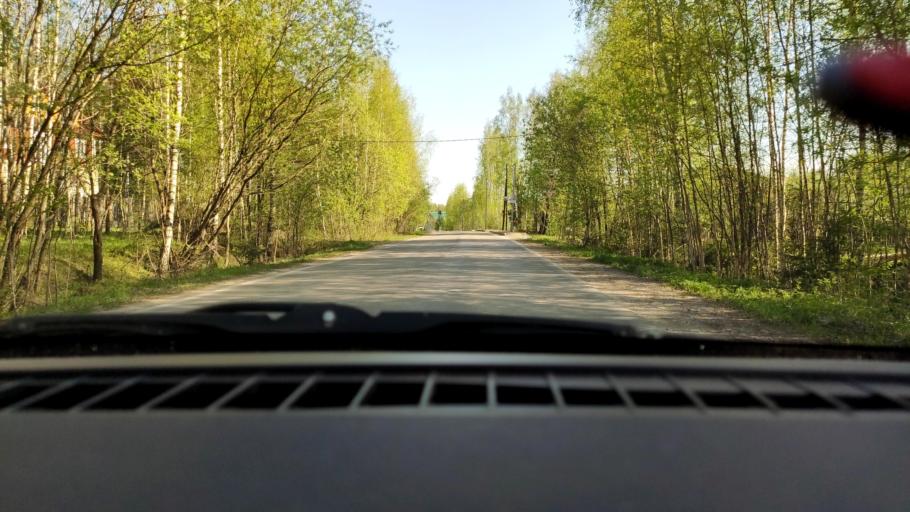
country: RU
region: Perm
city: Kondratovo
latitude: 58.0609
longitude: 56.0038
